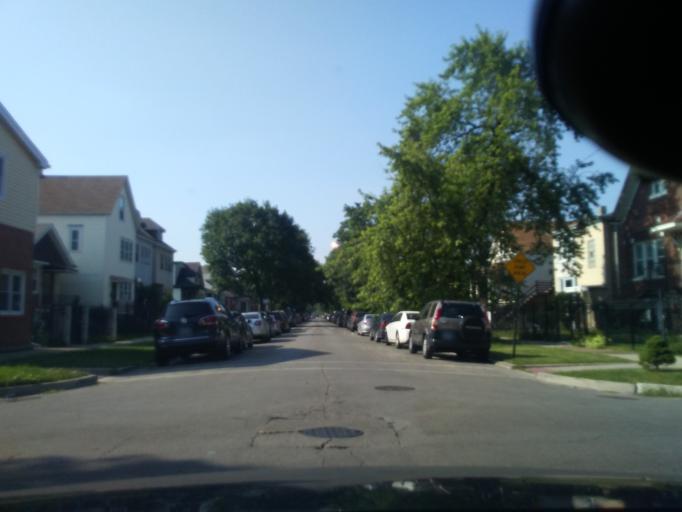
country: US
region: Illinois
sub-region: Cook County
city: Oak Park
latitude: 41.9222
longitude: -87.7672
